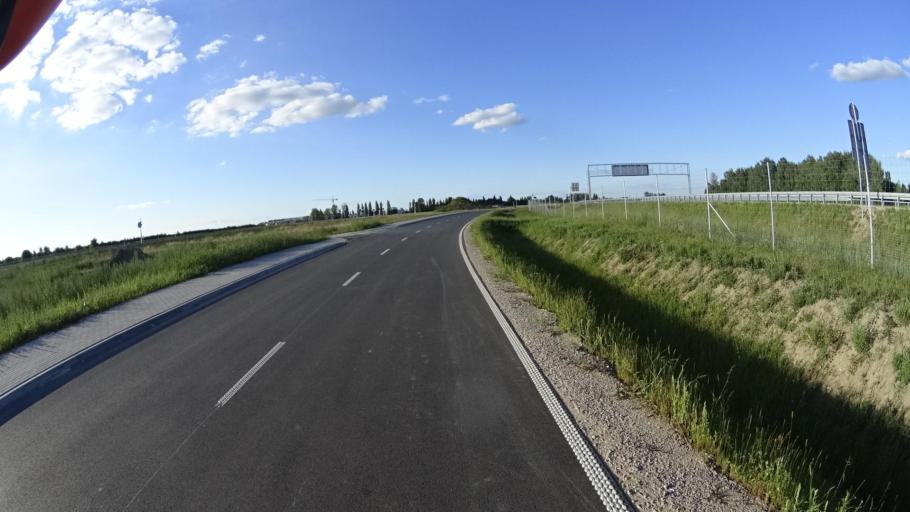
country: PL
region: Masovian Voivodeship
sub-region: Powiat piaseczynski
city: Lesznowola
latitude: 52.1035
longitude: 20.9696
